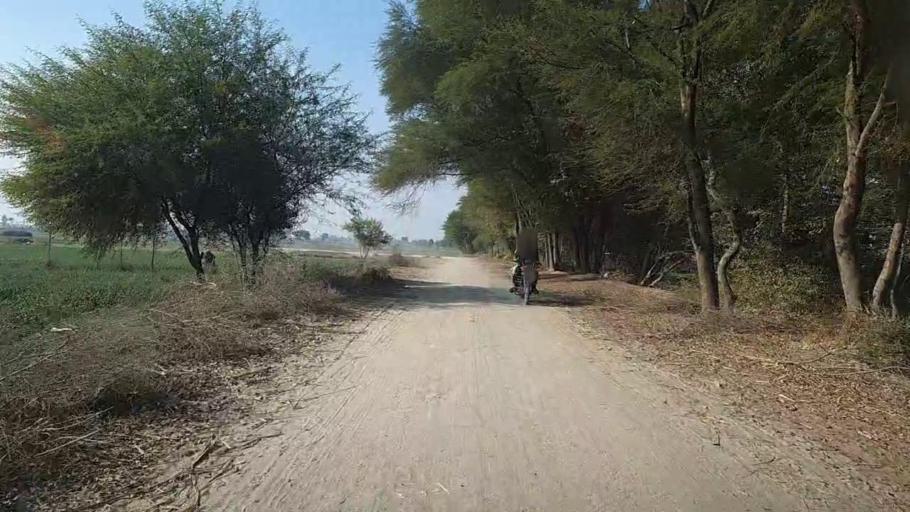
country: PK
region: Sindh
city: Mirpur Mathelo
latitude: 27.8983
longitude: 69.6499
